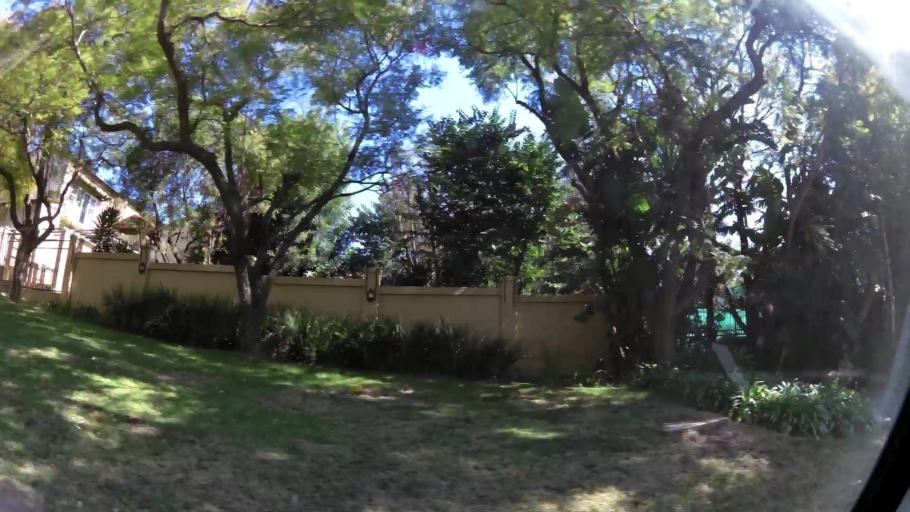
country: ZA
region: Gauteng
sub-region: City of Tshwane Metropolitan Municipality
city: Pretoria
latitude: -25.7917
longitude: 28.2406
